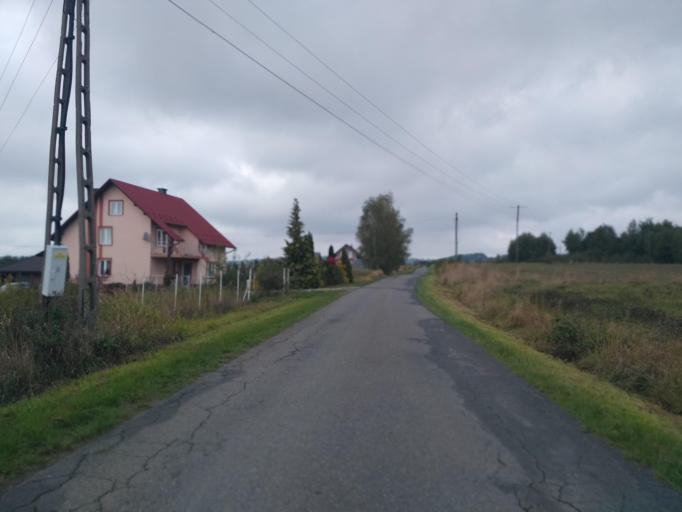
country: PL
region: Subcarpathian Voivodeship
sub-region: Powiat debicki
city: Brzostek
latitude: 49.9304
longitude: 21.4487
